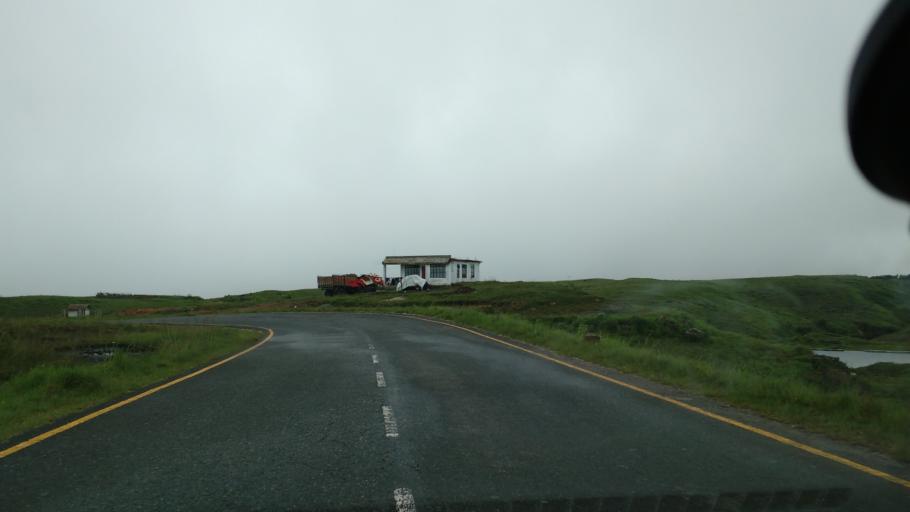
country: IN
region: Meghalaya
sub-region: East Khasi Hills
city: Cherrapunji
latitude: 25.3204
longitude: 91.7346
